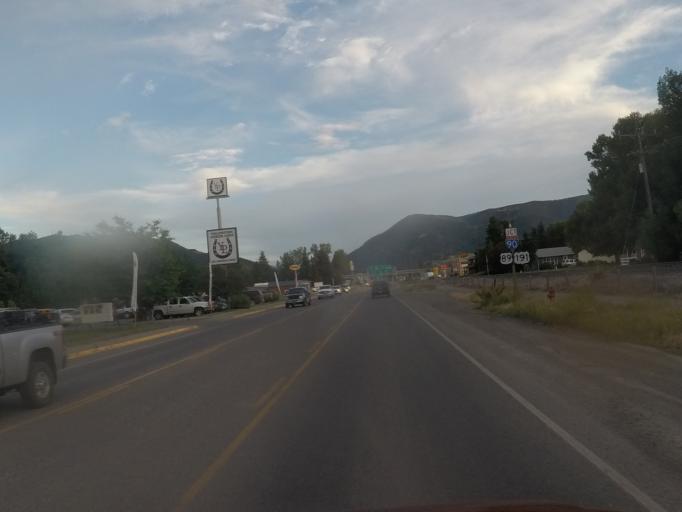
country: US
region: Montana
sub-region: Park County
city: Livingston
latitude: 45.6488
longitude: -110.5727
